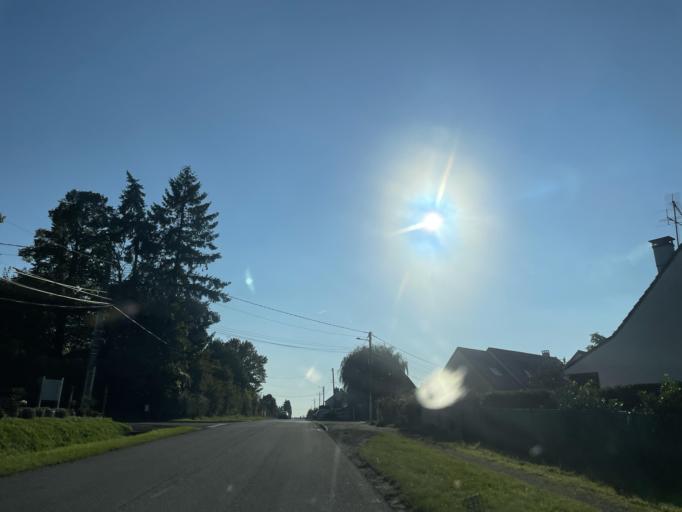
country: FR
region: Ile-de-France
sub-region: Departement de Seine-et-Marne
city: Voulangis
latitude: 48.8460
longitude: 2.8940
